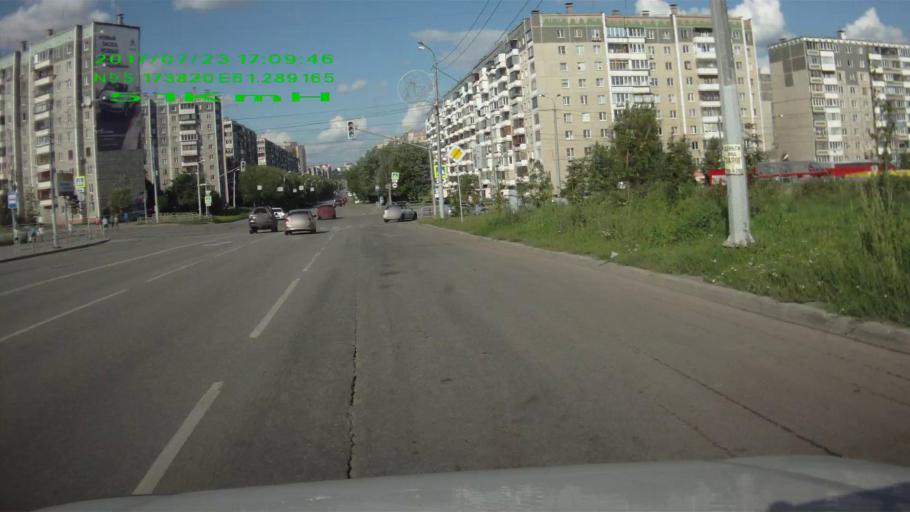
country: RU
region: Chelyabinsk
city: Roshchino
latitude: 55.1744
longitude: 61.2897
